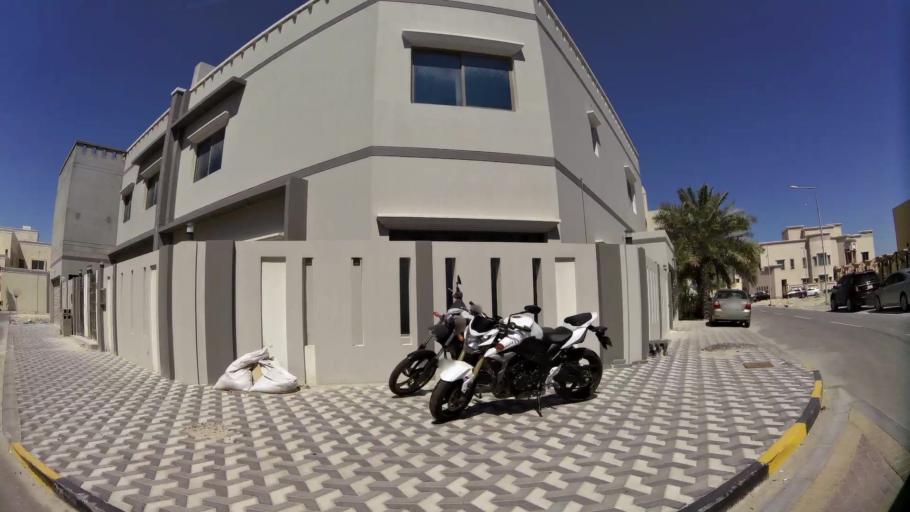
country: BH
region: Muharraq
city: Al Muharraq
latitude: 26.2791
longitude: 50.5989
